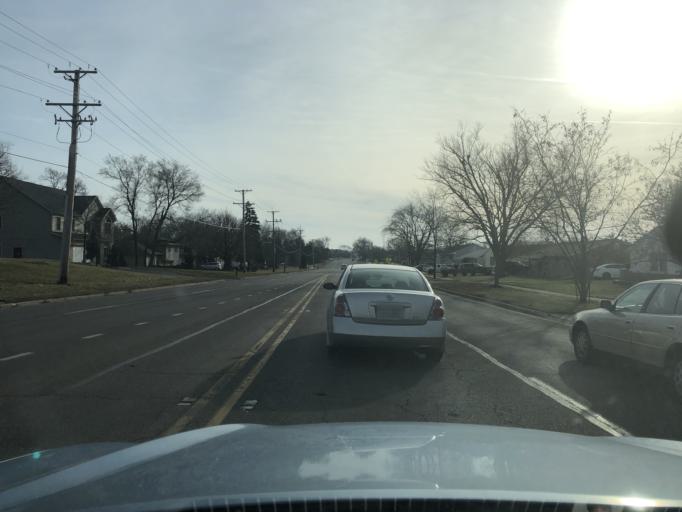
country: US
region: Illinois
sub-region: DuPage County
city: Glendale Heights
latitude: 41.9096
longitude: -88.0815
